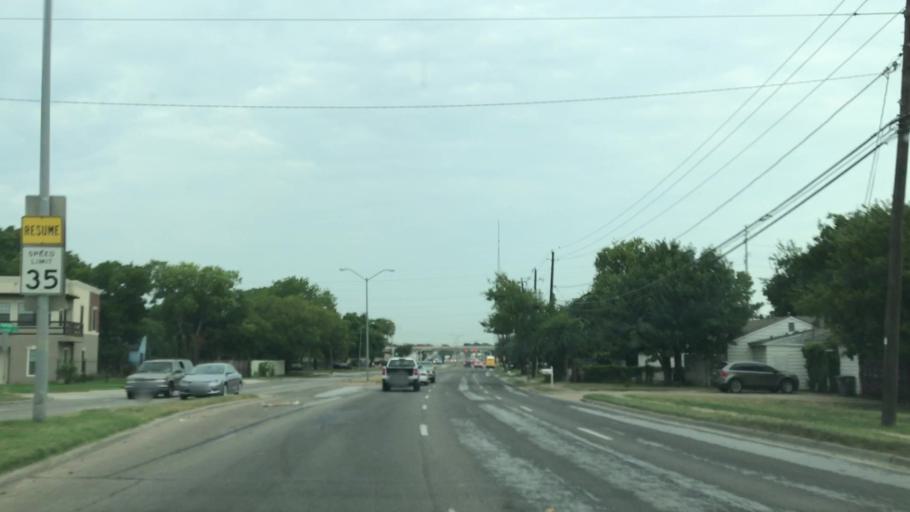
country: US
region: Texas
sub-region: Dallas County
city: Cockrell Hill
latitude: 32.7785
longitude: -96.9130
